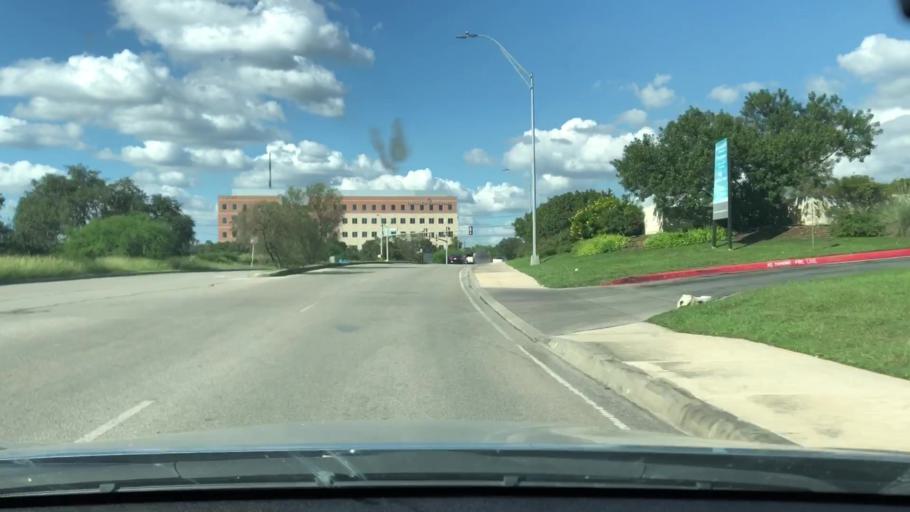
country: US
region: Texas
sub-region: Bexar County
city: Hollywood Park
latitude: 29.6137
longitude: -98.4785
